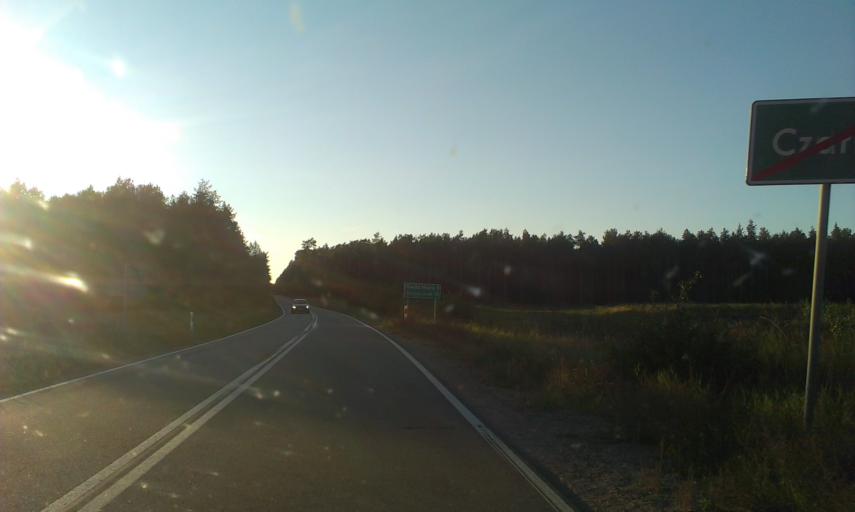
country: PL
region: Pomeranian Voivodeship
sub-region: Powiat czluchowski
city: Czarne
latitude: 53.6901
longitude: 16.9232
